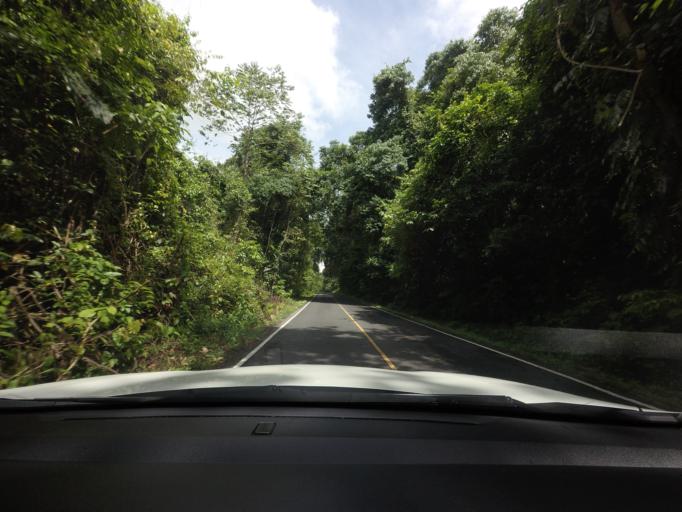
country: TH
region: Nakhon Nayok
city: Pak Phli
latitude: 14.3085
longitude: 101.3845
